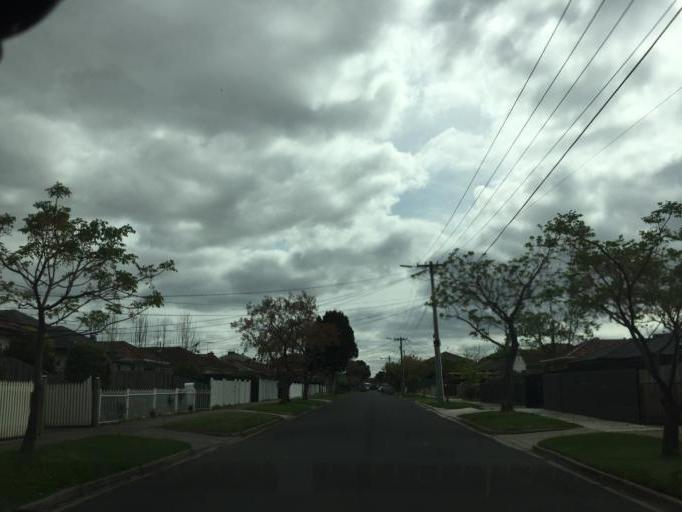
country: AU
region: Victoria
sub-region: Hobsons Bay
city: South Kingsville
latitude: -37.8159
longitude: 144.8656
